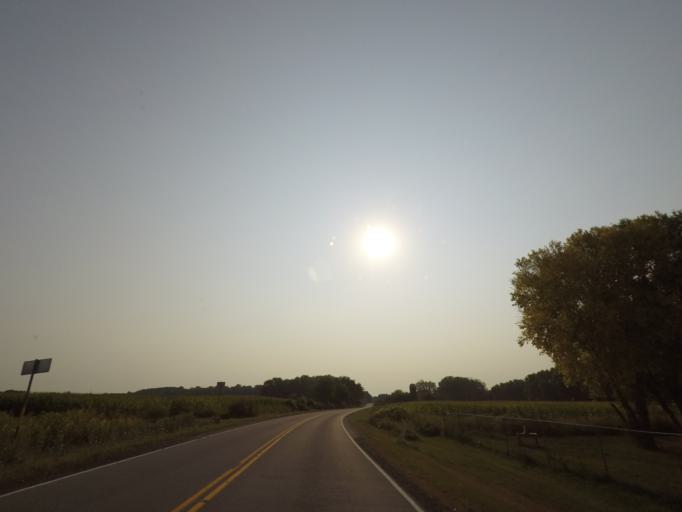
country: US
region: Wisconsin
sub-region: Dane County
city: McFarland
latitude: 43.0524
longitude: -89.2571
